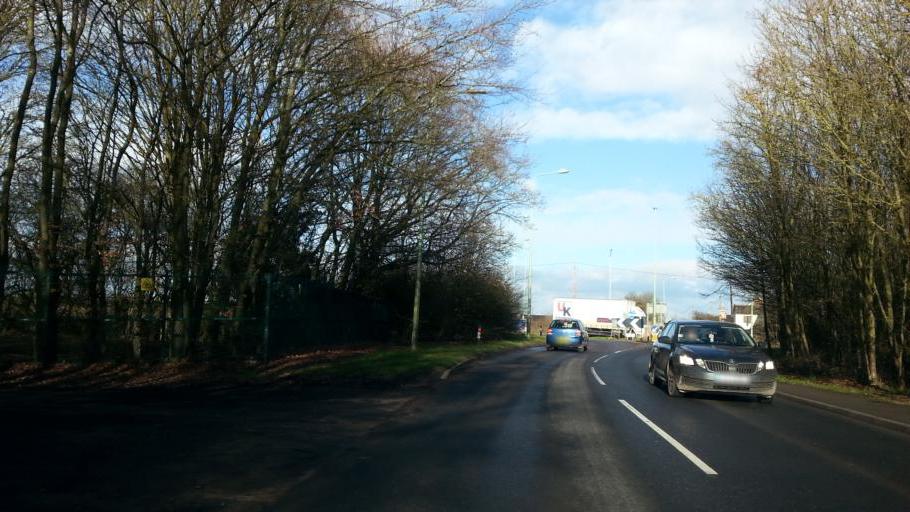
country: GB
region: England
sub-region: Suffolk
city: Halesworth
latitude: 52.3564
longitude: 1.5115
